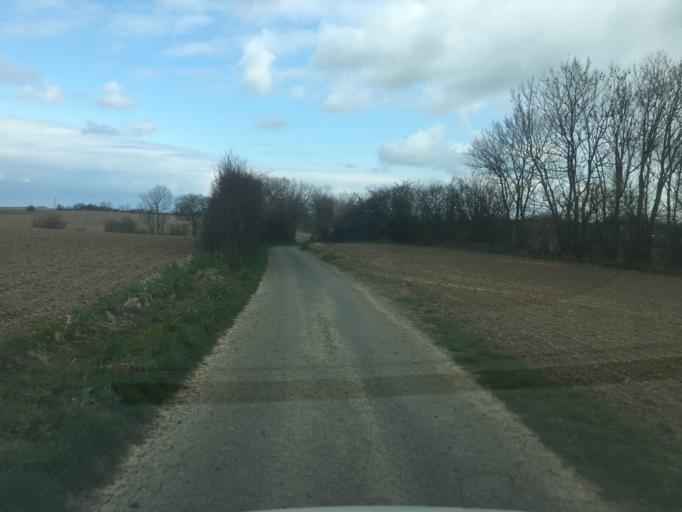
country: DK
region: South Denmark
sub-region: Sonderborg Kommune
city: Grasten
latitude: 54.9975
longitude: 9.5288
